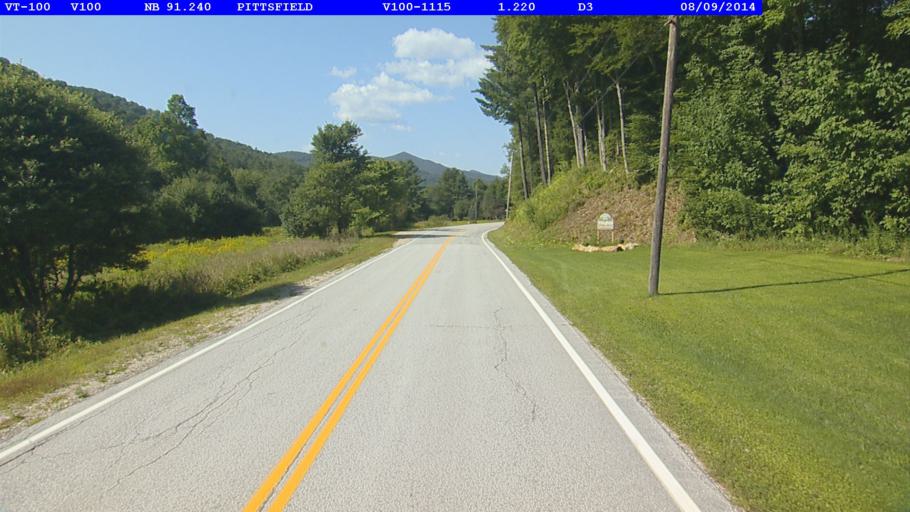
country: US
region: Vermont
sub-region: Rutland County
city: Rutland
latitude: 43.7346
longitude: -72.8207
